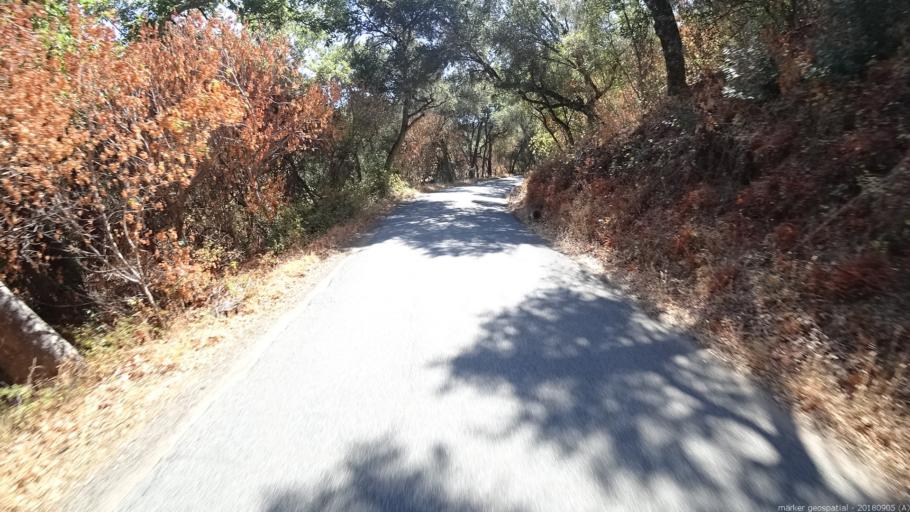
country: US
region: California
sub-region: Monterey County
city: Carmel Valley Village
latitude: 36.3935
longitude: -121.6085
